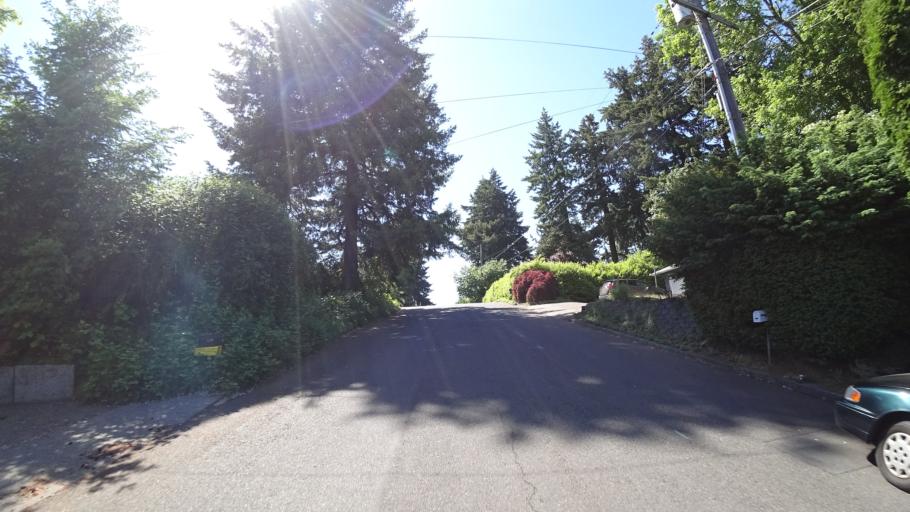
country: US
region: Oregon
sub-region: Washington County
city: Metzger
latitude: 45.4511
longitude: -122.7201
